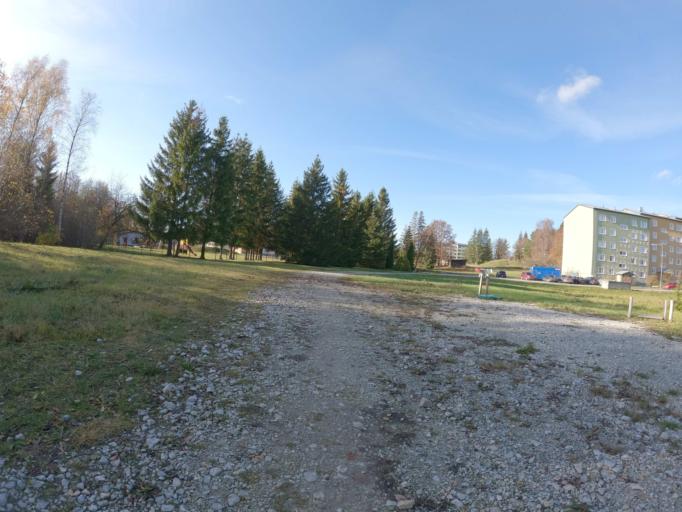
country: EE
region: Raplamaa
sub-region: Rapla vald
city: Rapla
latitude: 58.9977
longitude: 24.7965
